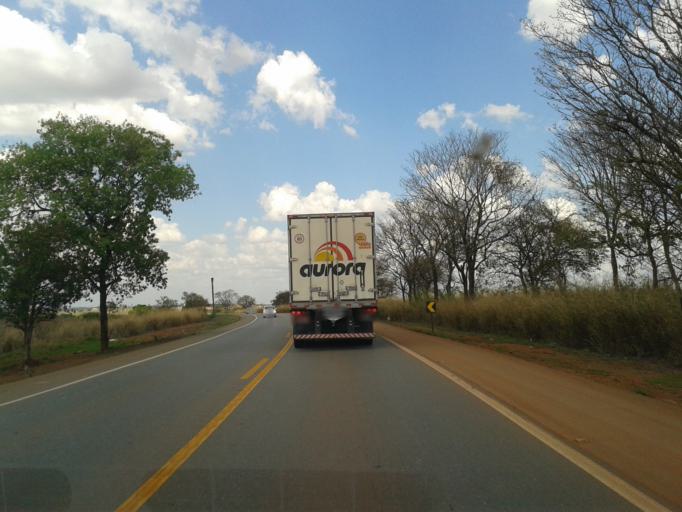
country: BR
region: Minas Gerais
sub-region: Luz
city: Luz
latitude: -19.7845
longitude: -45.7170
